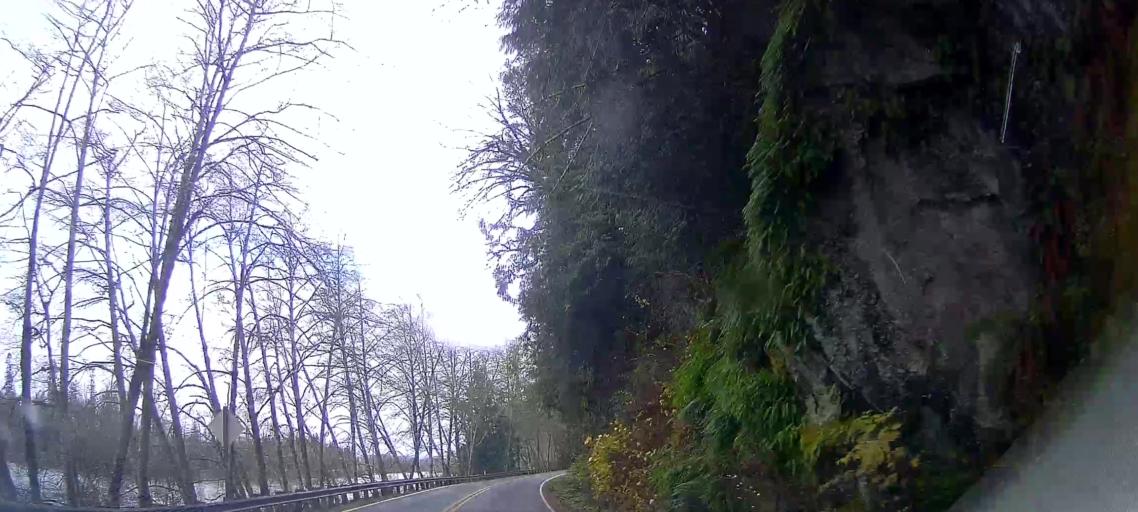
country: US
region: Washington
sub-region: Skagit County
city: Sedro-Woolley
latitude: 48.5145
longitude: -121.9854
